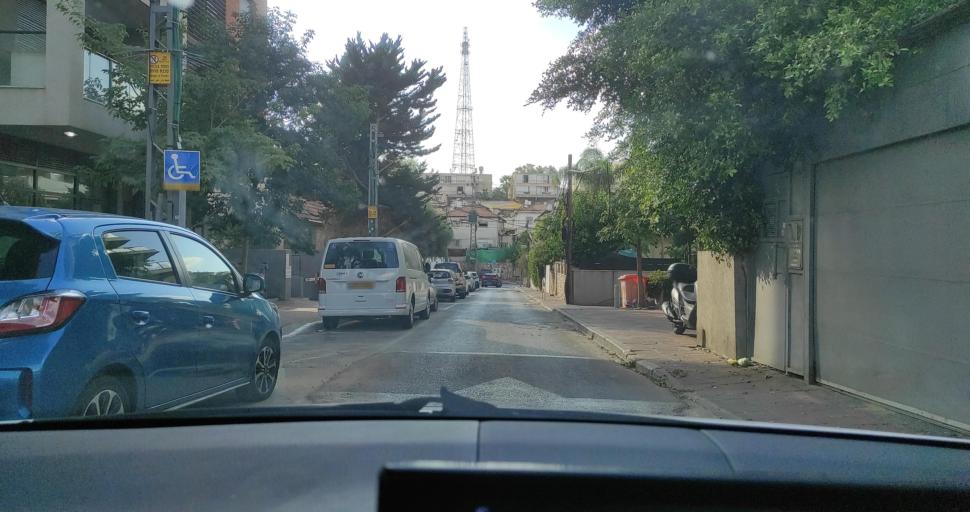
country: IL
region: Tel Aviv
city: Giv`atayim
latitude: 32.0721
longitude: 34.8193
